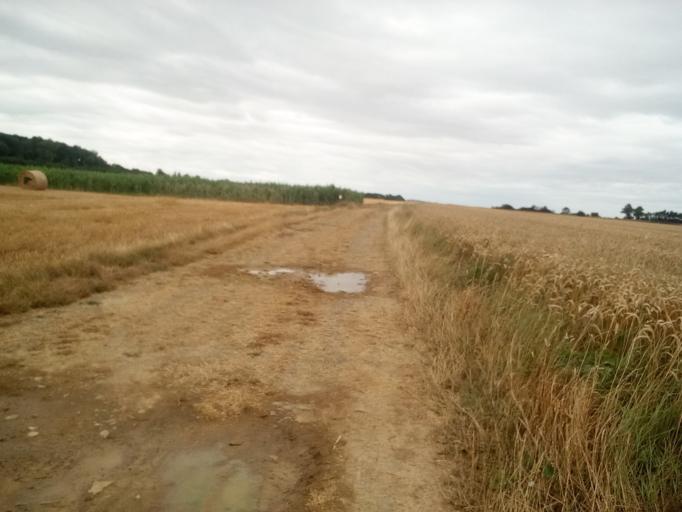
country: FR
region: Lower Normandy
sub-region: Departement du Calvados
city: Clinchamps-sur-Orne
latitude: 49.0555
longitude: -0.4107
